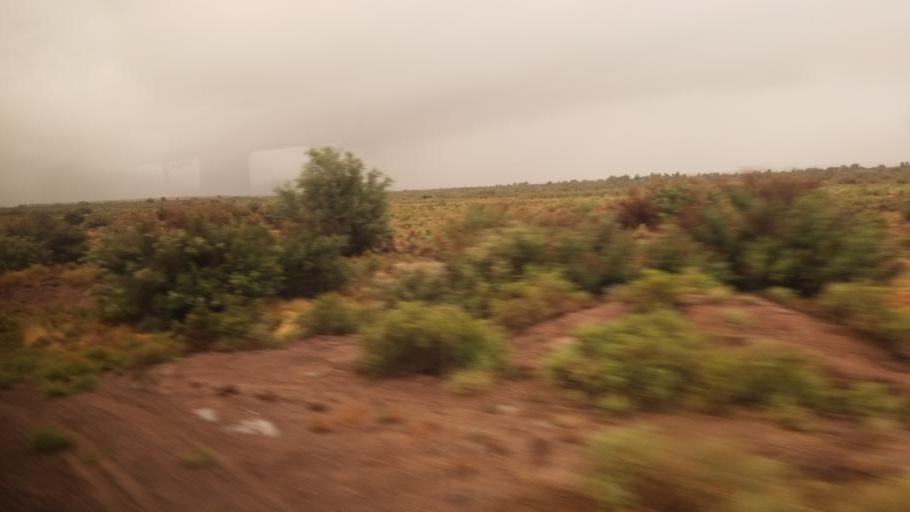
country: US
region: Arizona
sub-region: Navajo County
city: Joseph City
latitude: 34.9674
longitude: -110.4485
